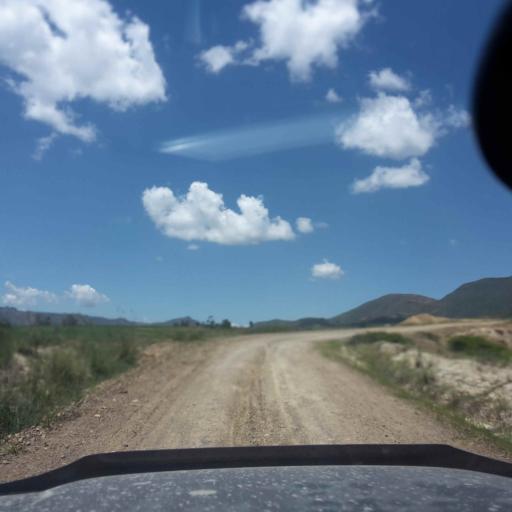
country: BO
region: Cochabamba
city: Totora
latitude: -17.7722
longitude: -65.2570
